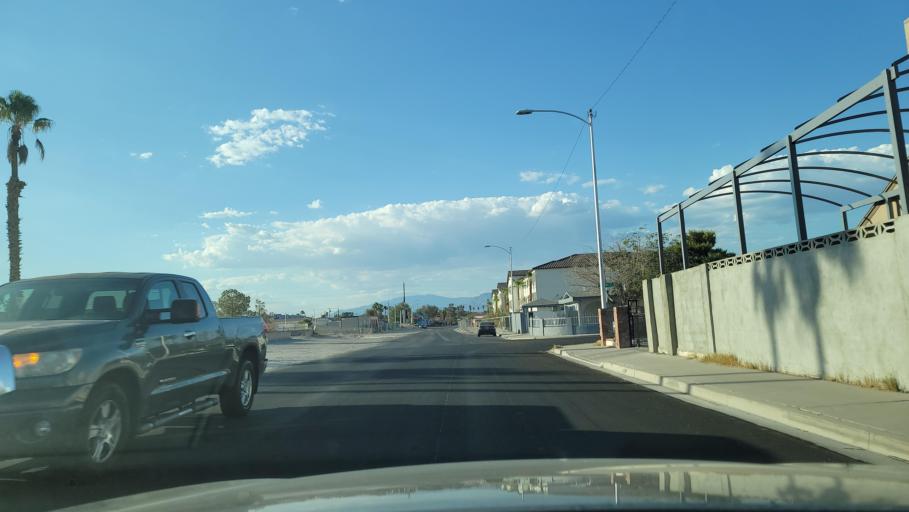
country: US
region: Nevada
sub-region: Clark County
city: Spring Valley
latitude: 36.1566
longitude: -115.2168
